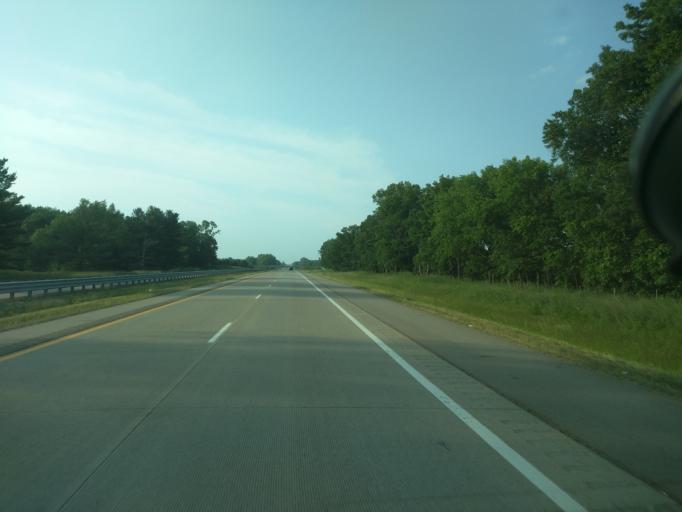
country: US
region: Michigan
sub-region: Jackson County
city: Jackson
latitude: 42.3429
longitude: -84.4288
